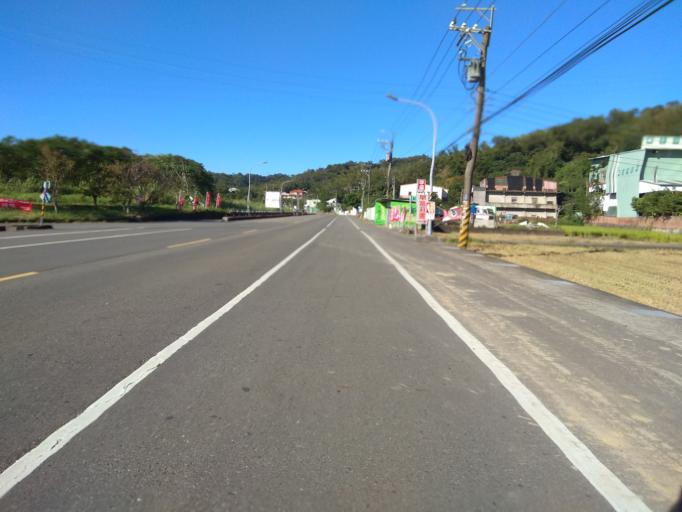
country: TW
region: Taiwan
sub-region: Hsinchu
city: Zhubei
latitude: 24.8483
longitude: 121.1110
